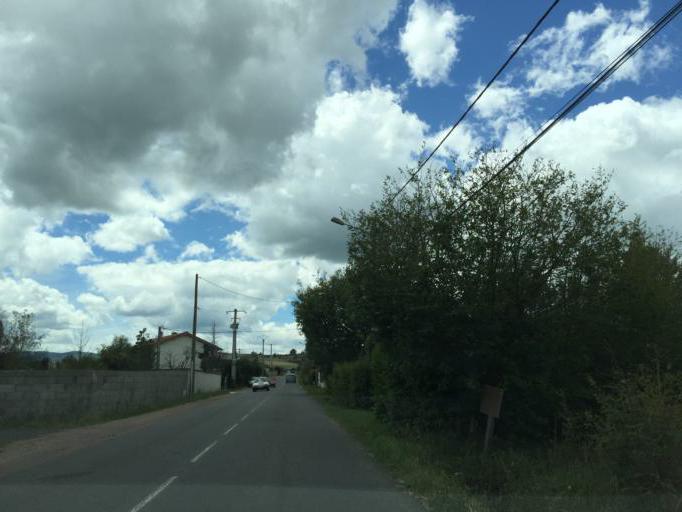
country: FR
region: Rhone-Alpes
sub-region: Departement de la Loire
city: Saint-Marcellin-en-Forez
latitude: 45.5008
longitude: 4.1579
